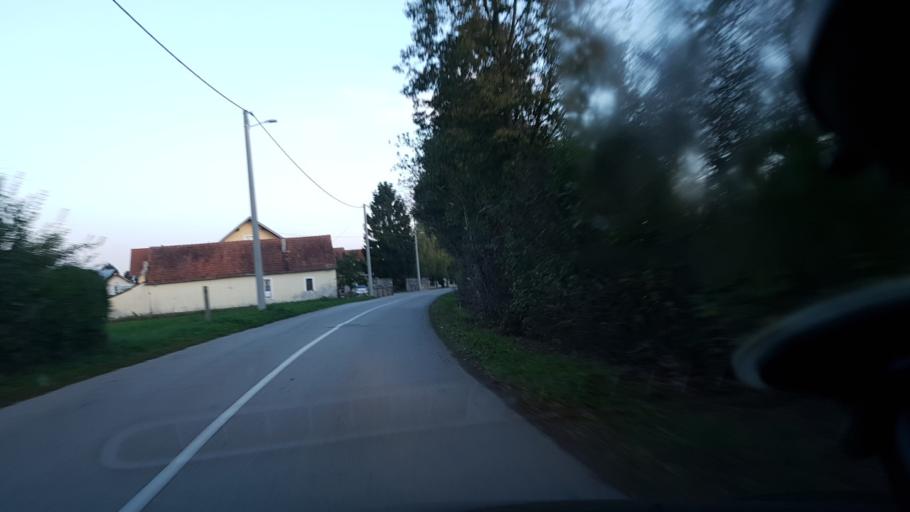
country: HR
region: Zagrebacka
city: Bregana
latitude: 45.8691
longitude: 15.7109
